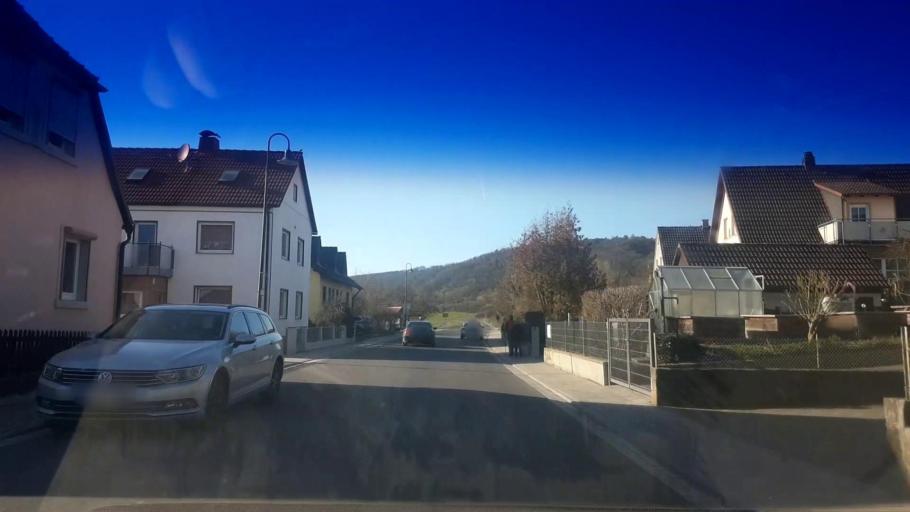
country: DE
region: Bavaria
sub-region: Regierungsbezirk Unterfranken
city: Stettfeld
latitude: 49.9707
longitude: 10.7195
